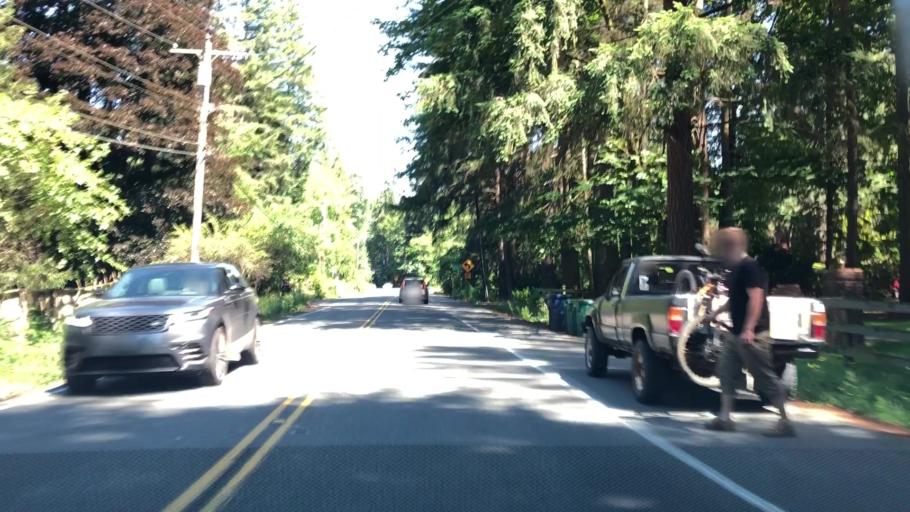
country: US
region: Washington
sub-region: King County
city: Cottage Lake
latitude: 47.7176
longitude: -122.0861
